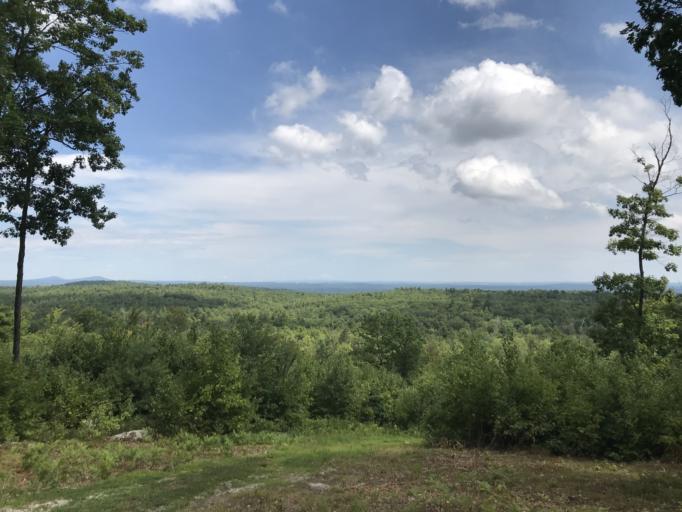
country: US
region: New Hampshire
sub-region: Hillsborough County
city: Brookline
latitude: 42.7783
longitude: -71.6372
